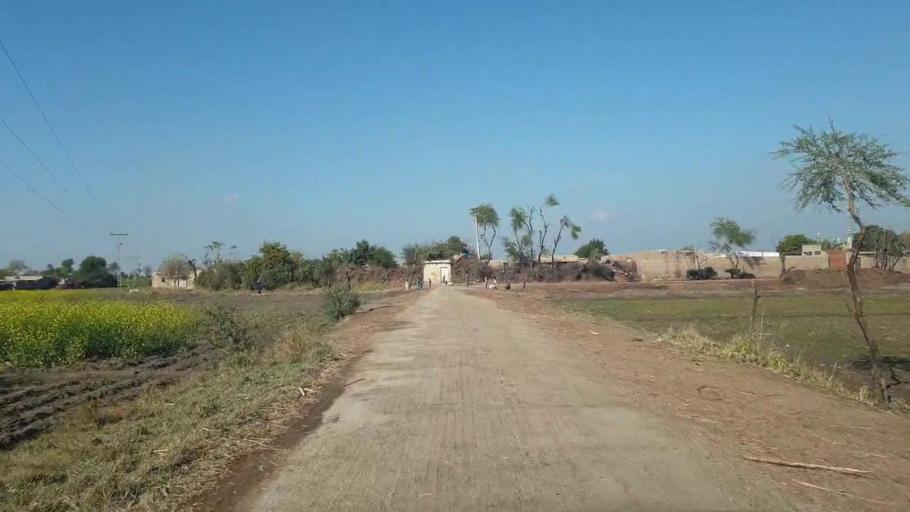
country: PK
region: Sindh
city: Shahdadpur
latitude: 25.9323
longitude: 68.5302
